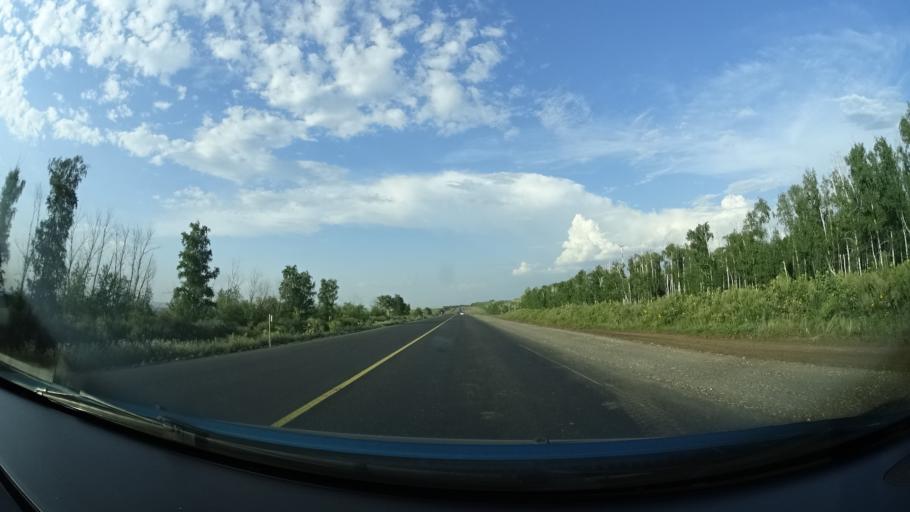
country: RU
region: Samara
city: Sukhodol
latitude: 53.7576
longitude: 50.8770
